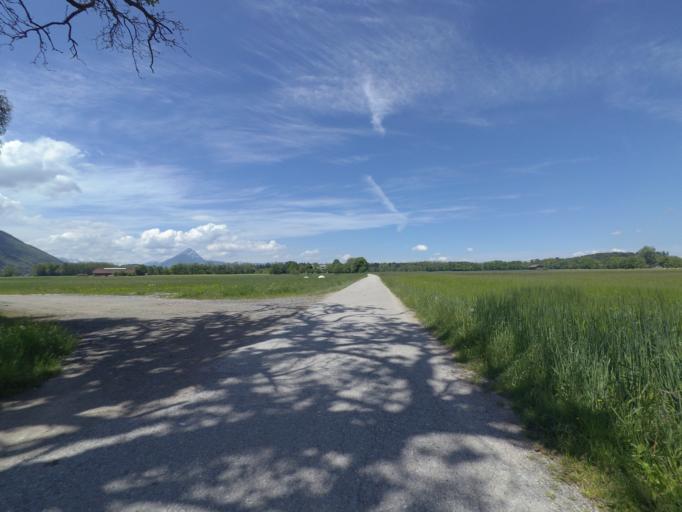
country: AT
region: Salzburg
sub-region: Politischer Bezirk Salzburg-Umgebung
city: Anif
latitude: 47.7540
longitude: 13.0581
